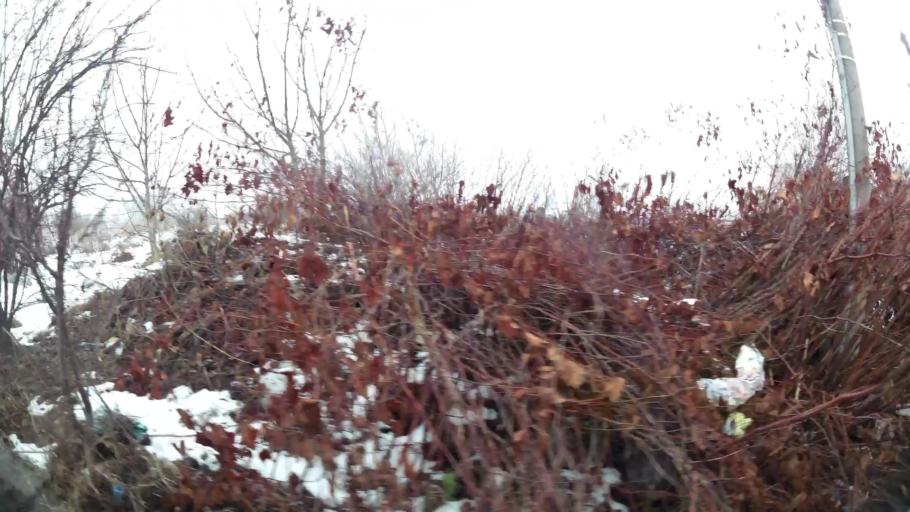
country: RO
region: Ilfov
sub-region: Comuna Chiajna
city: Rosu
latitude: 44.4472
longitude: 26.0280
